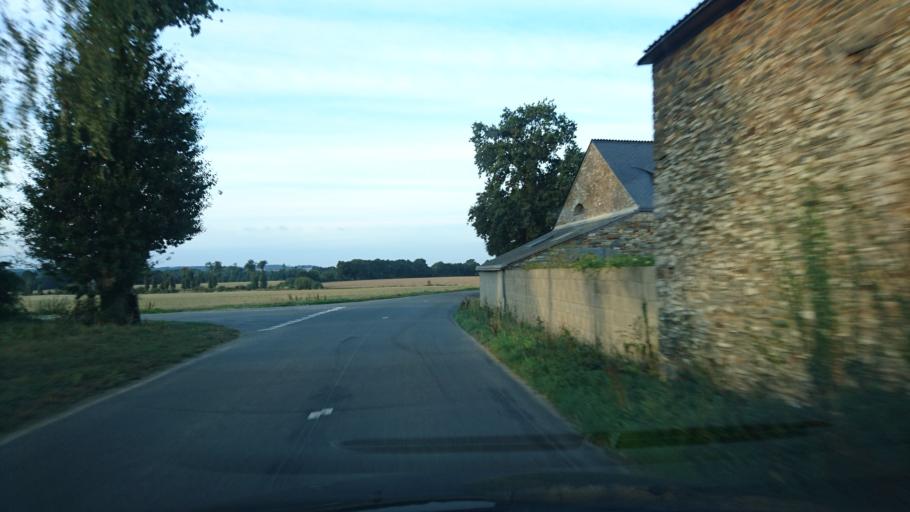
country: FR
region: Brittany
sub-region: Departement d'Ille-et-Vilaine
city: Sixt-sur-Aff
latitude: 47.7805
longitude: -2.0741
